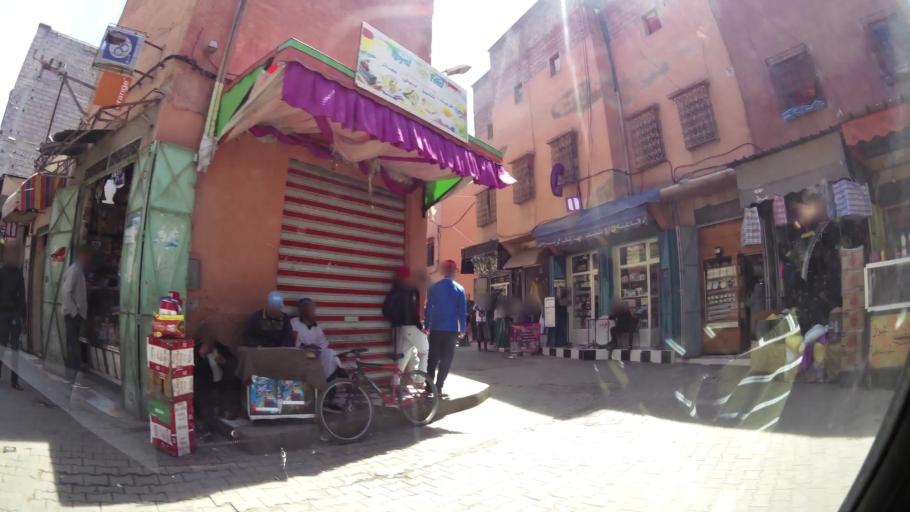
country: MA
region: Marrakech-Tensift-Al Haouz
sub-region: Marrakech
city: Marrakesh
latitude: 31.6176
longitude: -7.9684
